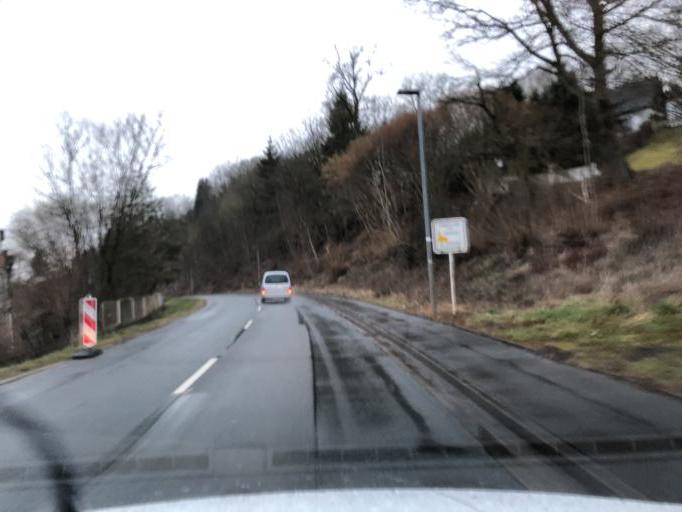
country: DE
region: Lower Saxony
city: Rhumspringe
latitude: 51.5907
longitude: 10.3086
